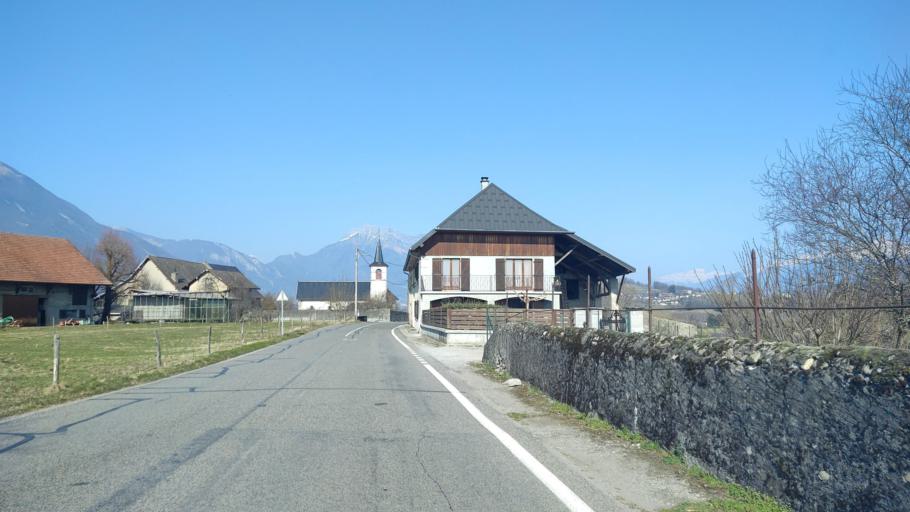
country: FR
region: Rhone-Alpes
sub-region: Departement de la Savoie
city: Cruet
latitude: 45.4995
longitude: 6.0868
